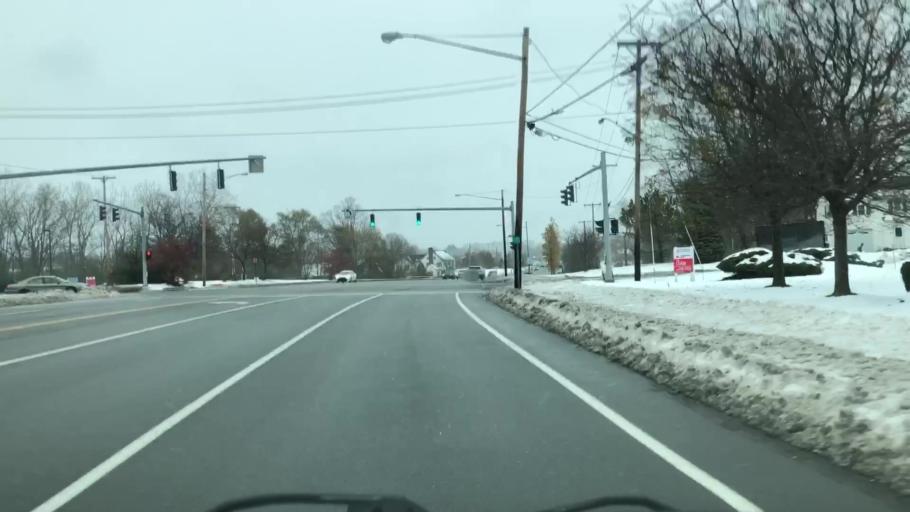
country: US
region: New York
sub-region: Monroe County
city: North Gates
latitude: 43.1299
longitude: -77.6946
